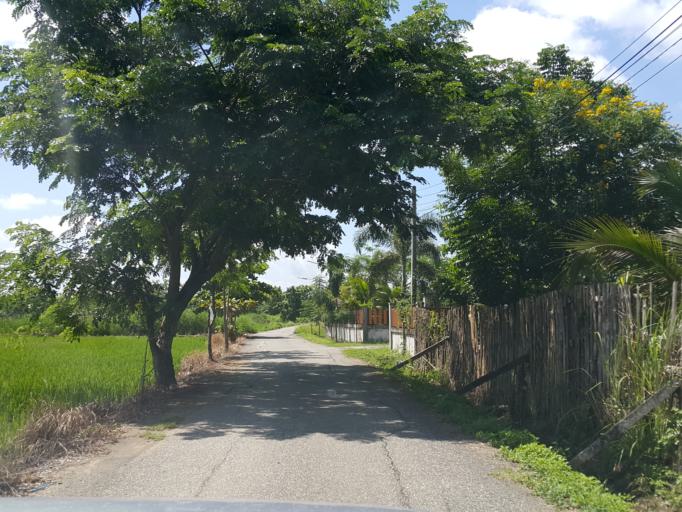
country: TH
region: Chiang Mai
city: San Kamphaeng
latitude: 18.7190
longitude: 99.1066
